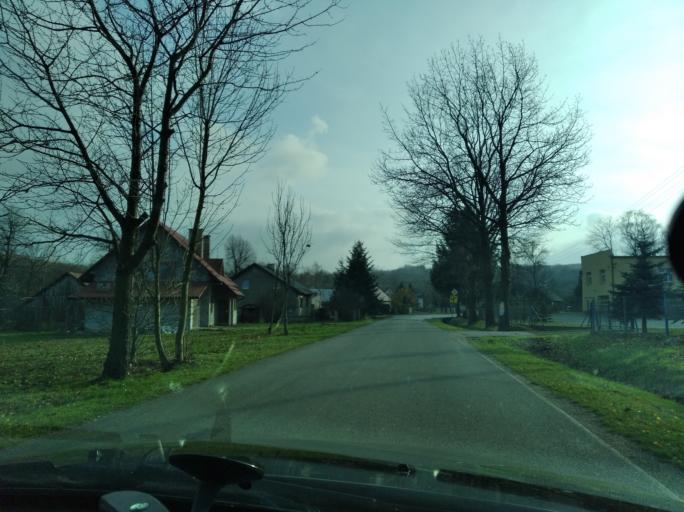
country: PL
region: Subcarpathian Voivodeship
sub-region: Powiat przeworski
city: Lopuszka Wielka
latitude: 49.9433
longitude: 22.4043
